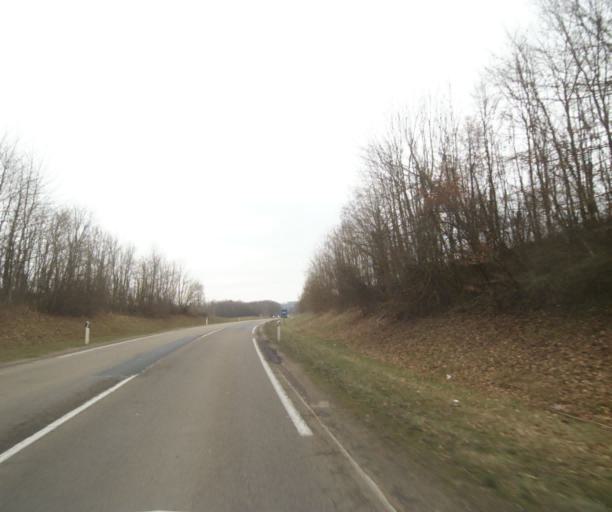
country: FR
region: Champagne-Ardenne
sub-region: Departement de la Haute-Marne
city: Bienville
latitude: 48.5758
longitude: 5.0354
